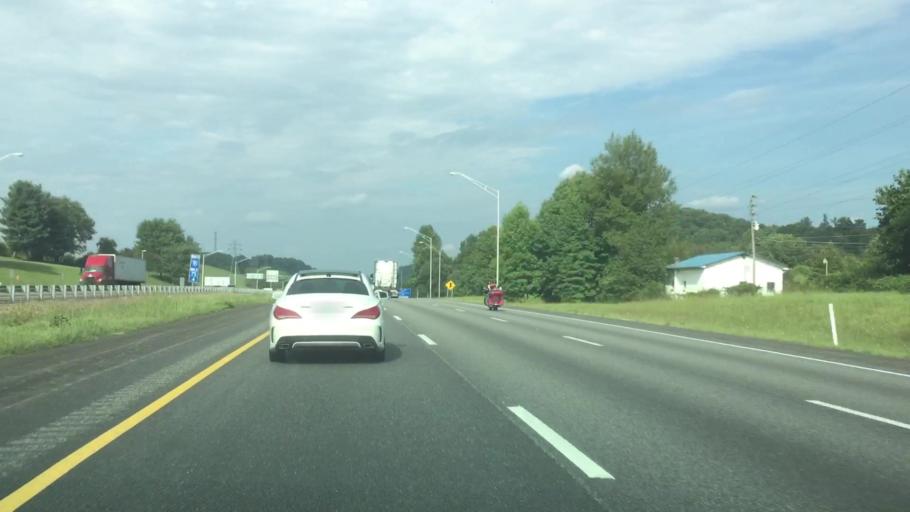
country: US
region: Tennessee
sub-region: Sullivan County
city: Walnut Hill
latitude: 36.5939
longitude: -82.2474
